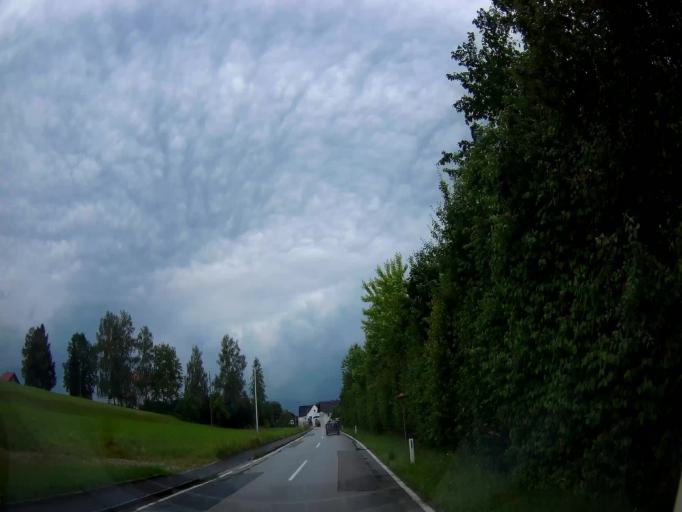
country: AT
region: Salzburg
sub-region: Politischer Bezirk Salzburg-Umgebung
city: Mattsee
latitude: 48.0807
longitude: 13.1460
